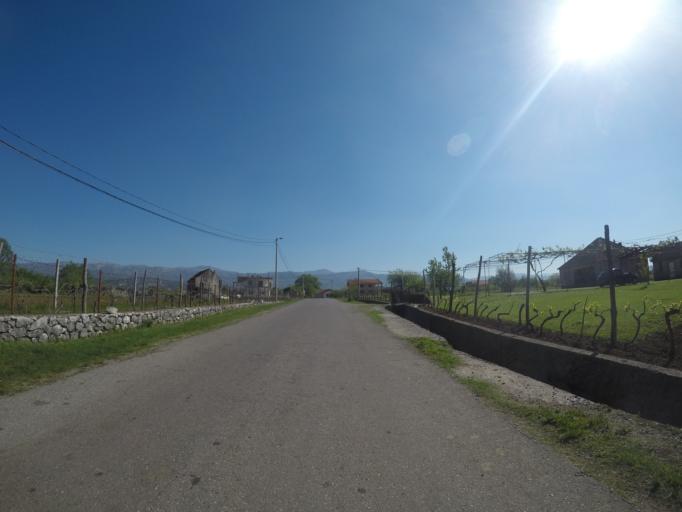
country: ME
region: Danilovgrad
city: Danilovgrad
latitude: 42.5383
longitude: 19.0912
